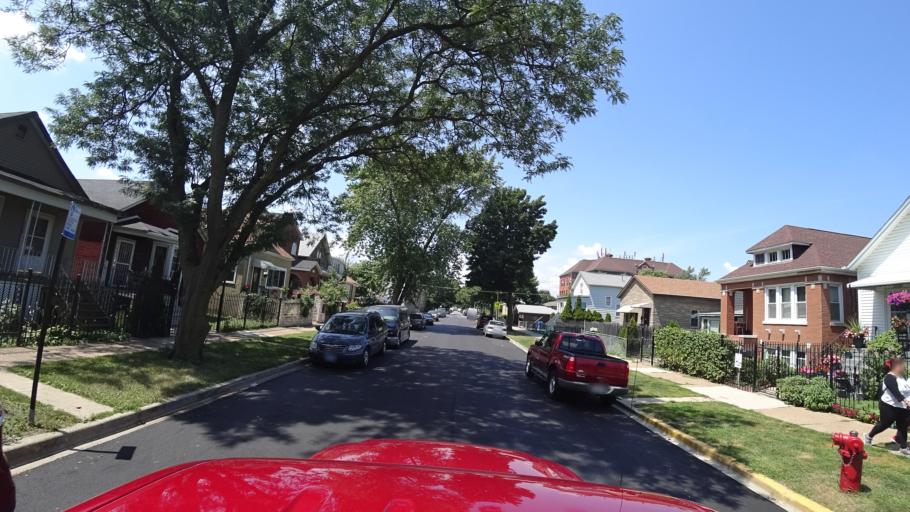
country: US
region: Illinois
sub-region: Cook County
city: Chicago
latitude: 41.8284
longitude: -87.6910
